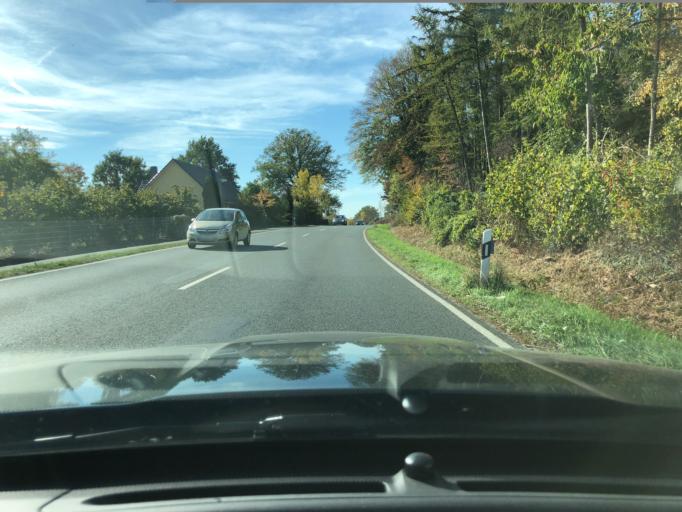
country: DE
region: Lower Saxony
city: Hagen
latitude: 52.2482
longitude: 7.9843
